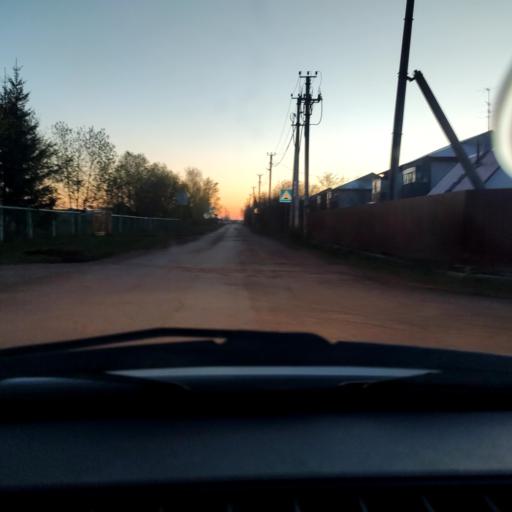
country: RU
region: Bashkortostan
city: Mikhaylovka
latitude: 54.8660
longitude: 55.7383
